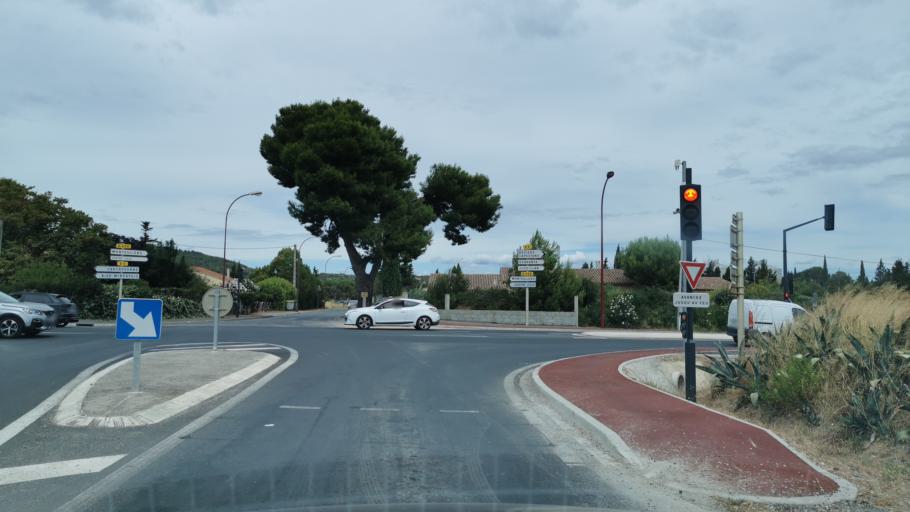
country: FR
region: Languedoc-Roussillon
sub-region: Departement de l'Aude
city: Argeliers
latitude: 43.3049
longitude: 2.9104
